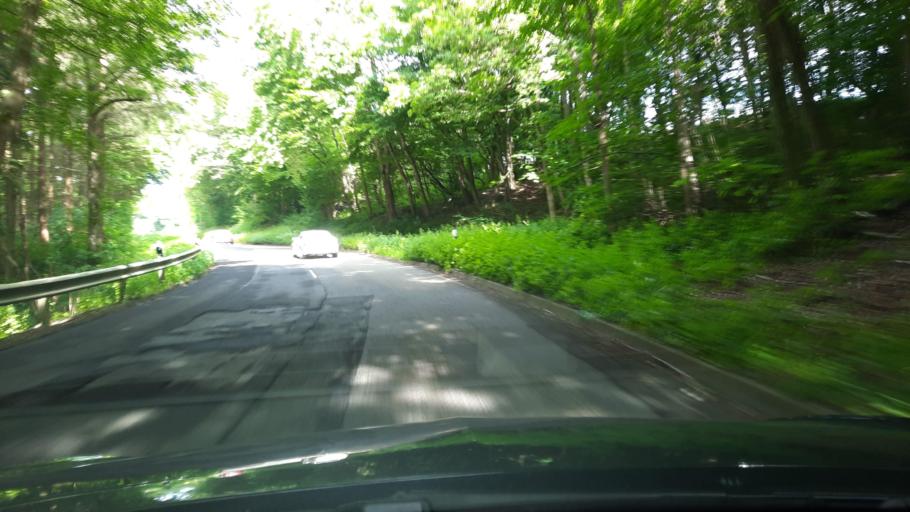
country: DE
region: Rheinland-Pfalz
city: Spessart
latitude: 50.4459
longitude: 7.1294
